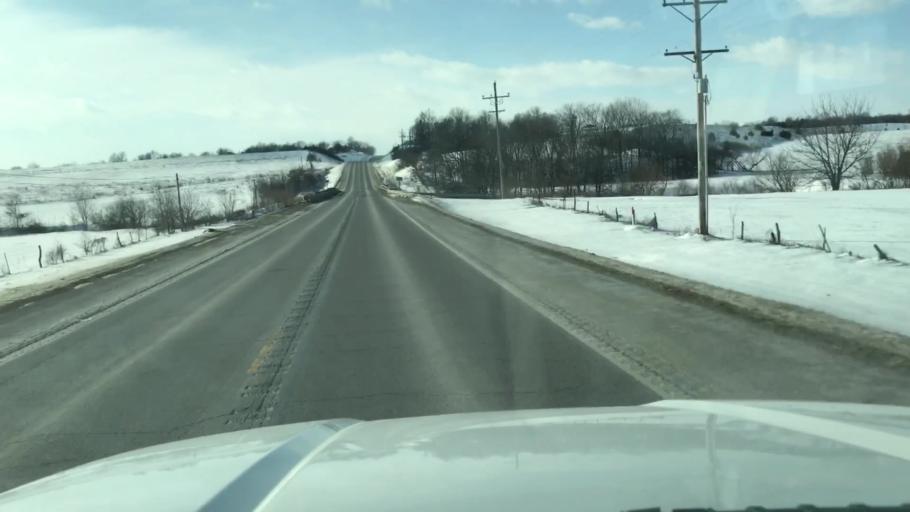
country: US
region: Missouri
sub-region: Nodaway County
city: Maryville
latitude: 40.3445
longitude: -94.7782
